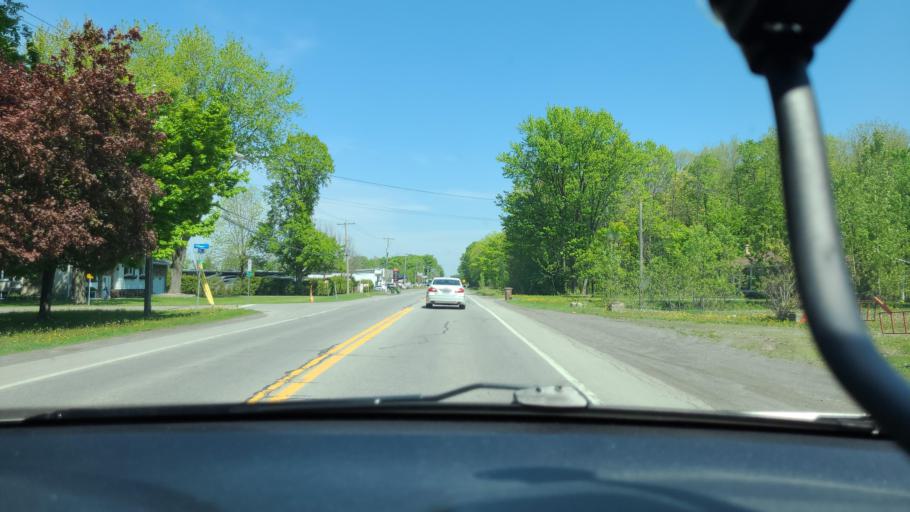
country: CA
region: Quebec
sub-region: Laurentides
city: Saint-Eustache
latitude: 45.5852
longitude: -73.9449
